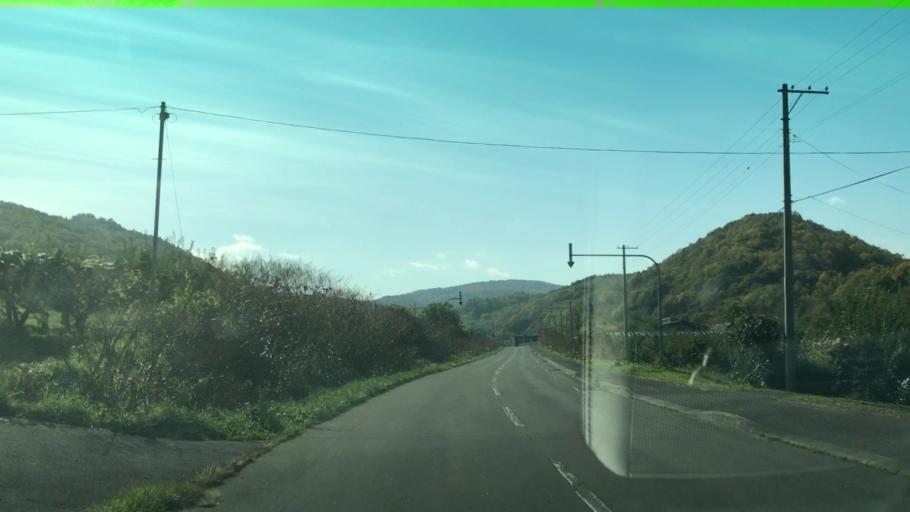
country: JP
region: Hokkaido
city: Yoichi
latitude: 43.1569
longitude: 140.8221
